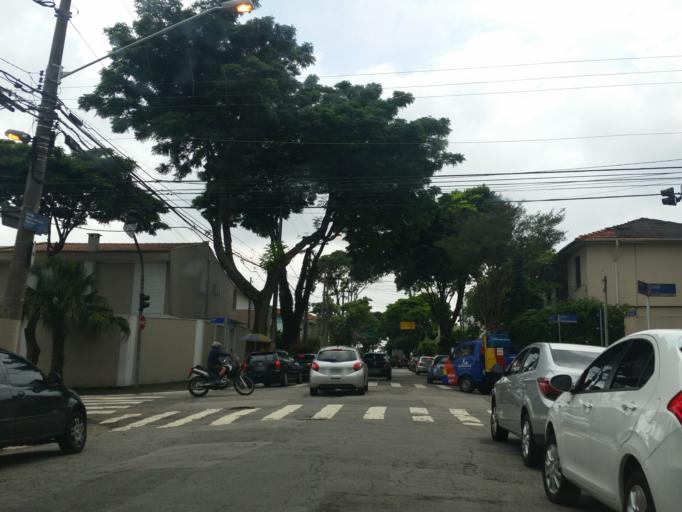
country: BR
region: Sao Paulo
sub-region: Diadema
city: Diadema
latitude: -23.6191
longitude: -46.6496
